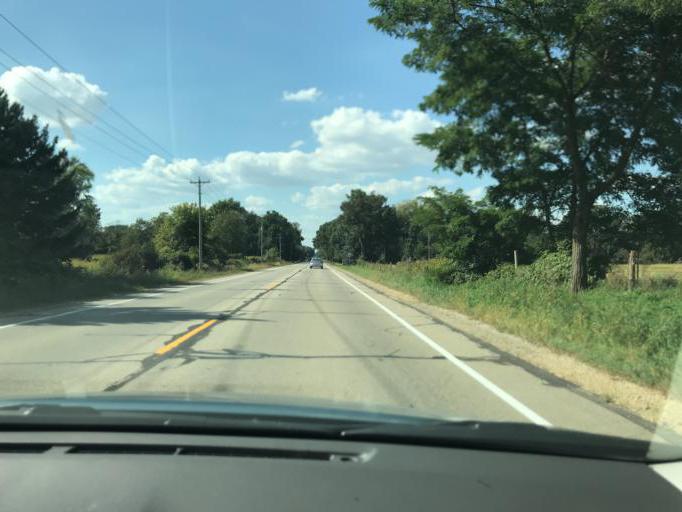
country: US
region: Wisconsin
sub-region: Walworth County
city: Williams Bay
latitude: 42.6062
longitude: -88.5542
